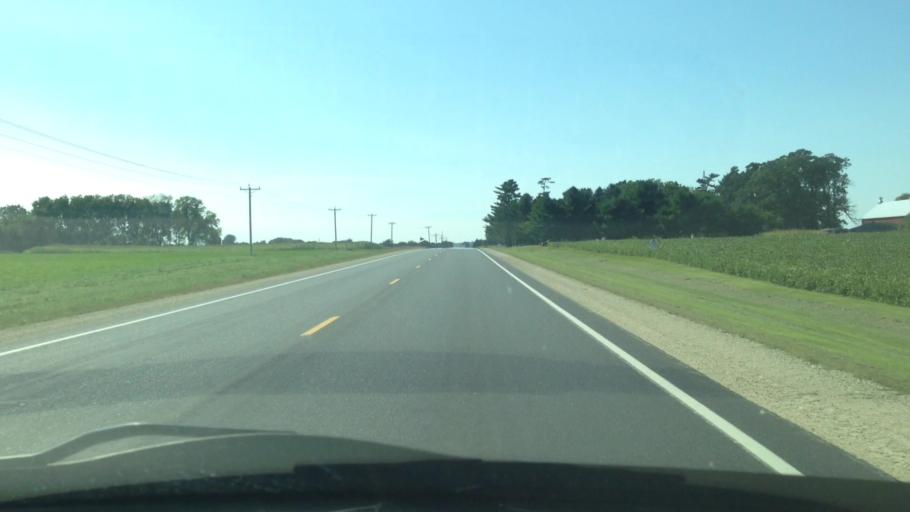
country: US
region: Minnesota
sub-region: Winona County
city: Lewiston
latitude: 43.9697
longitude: -91.8501
